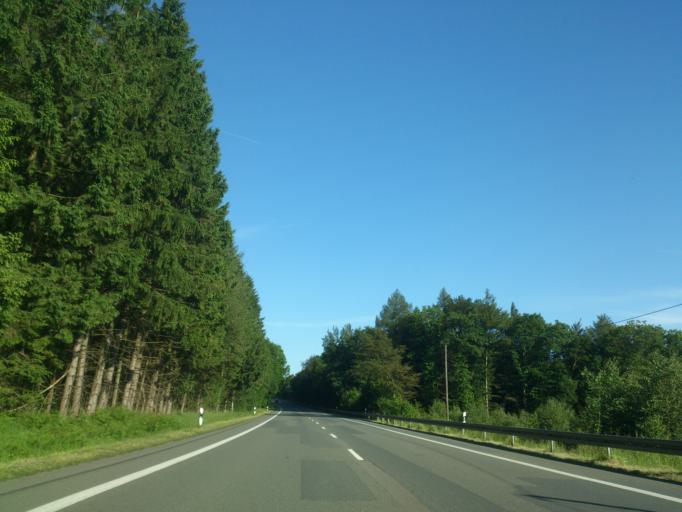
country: DE
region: North Rhine-Westphalia
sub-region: Regierungsbezirk Detmold
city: Altenbeken
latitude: 51.6955
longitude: 8.9576
